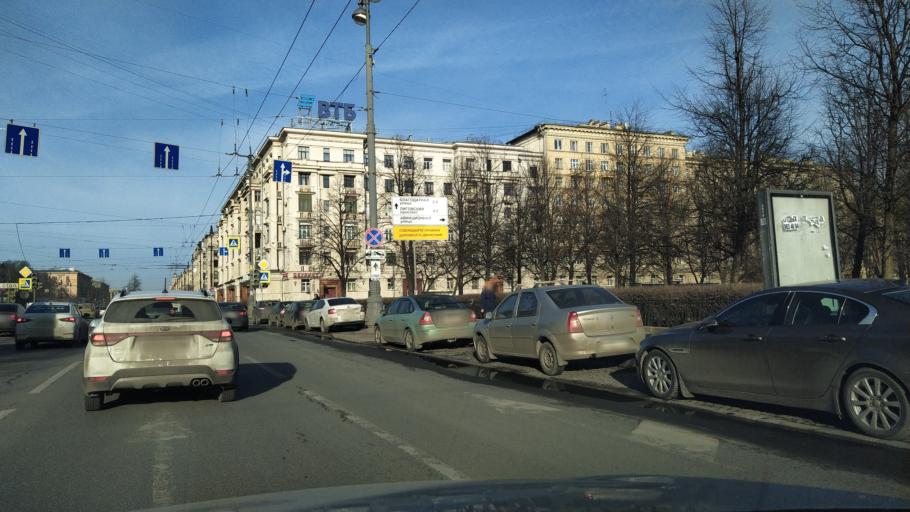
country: RU
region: St.-Petersburg
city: Kupchino
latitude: 59.8542
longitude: 30.3215
